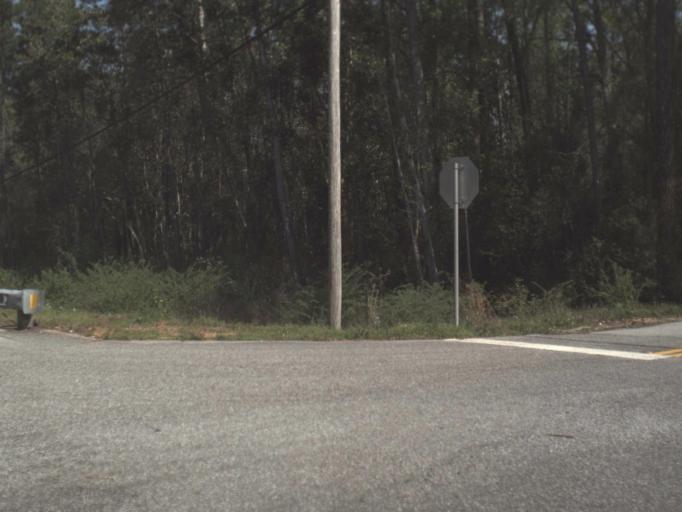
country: US
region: Alabama
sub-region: Escambia County
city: East Brewton
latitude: 30.9204
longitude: -87.0476
